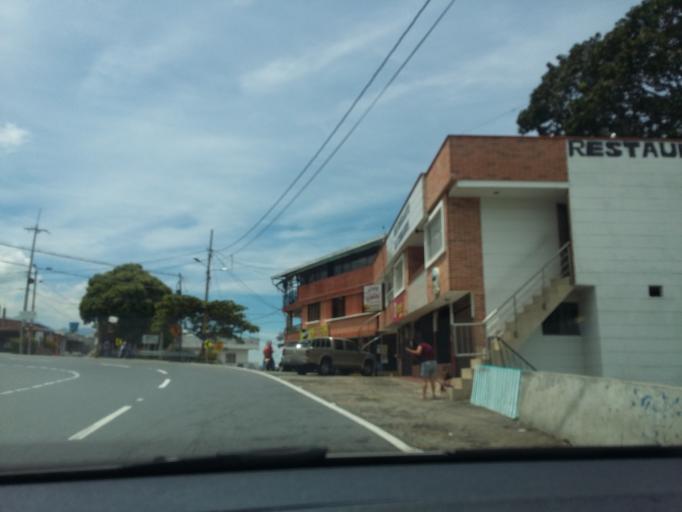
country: CO
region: Santander
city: Bucaramanga
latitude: 7.1112
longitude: -73.0832
